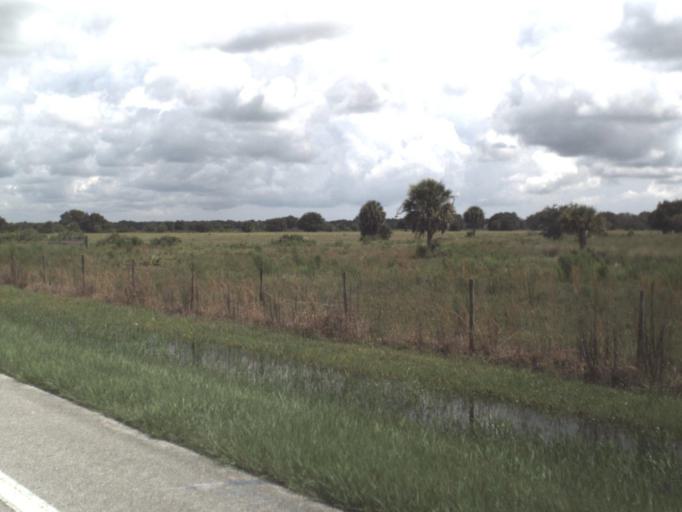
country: US
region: Florida
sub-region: Sarasota County
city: Warm Mineral Springs
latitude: 27.1935
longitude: -82.1722
